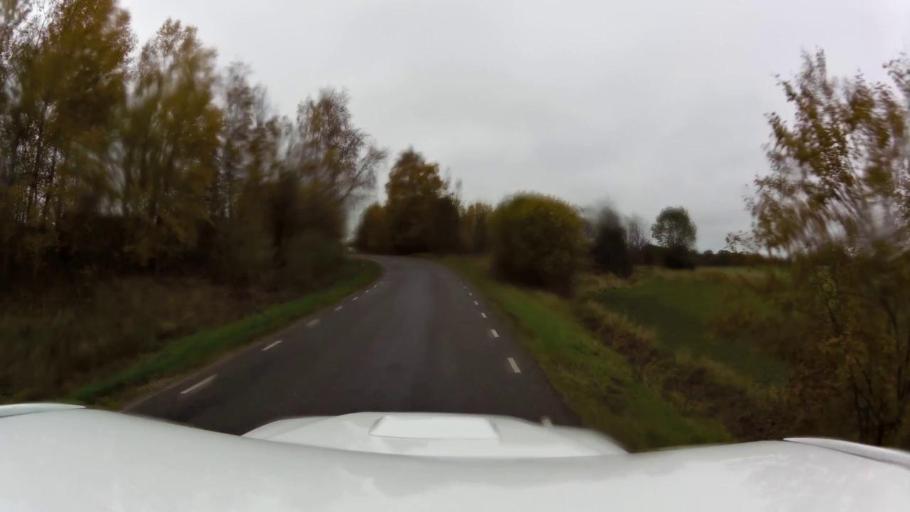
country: SE
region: OEstergoetland
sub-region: Linkopings Kommun
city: Linghem
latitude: 58.4753
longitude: 15.7234
